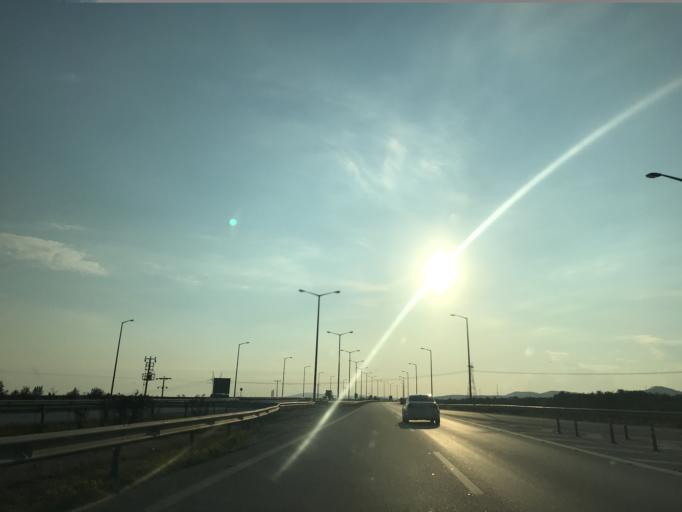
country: TR
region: Osmaniye
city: Toprakkale
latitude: 36.9707
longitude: 36.0571
